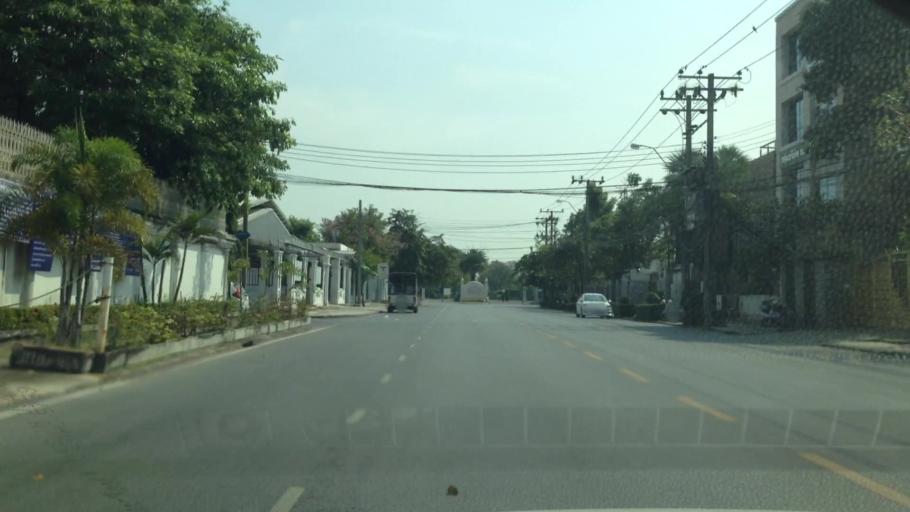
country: TH
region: Bangkok
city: Bang Na
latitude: 13.6884
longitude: 100.6568
